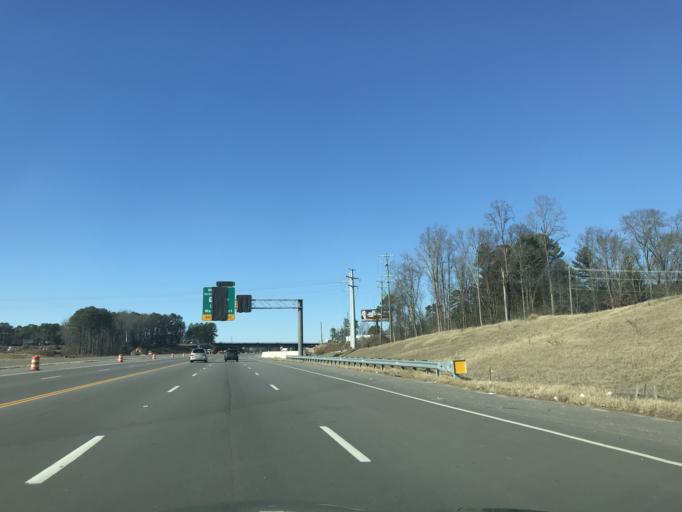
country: US
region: North Carolina
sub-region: Durham County
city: Durham
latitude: 35.9813
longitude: -78.8570
